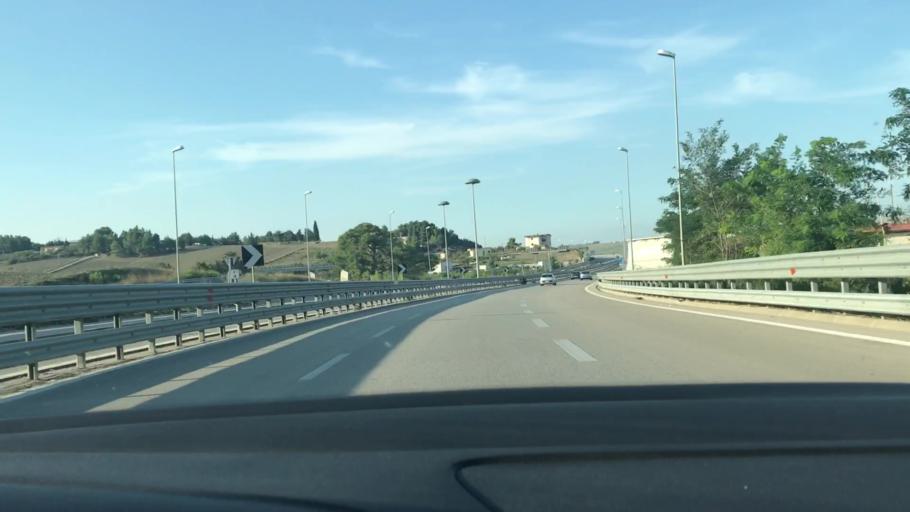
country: IT
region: Basilicate
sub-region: Provincia di Matera
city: Matera
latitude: 40.6886
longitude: 16.5901
